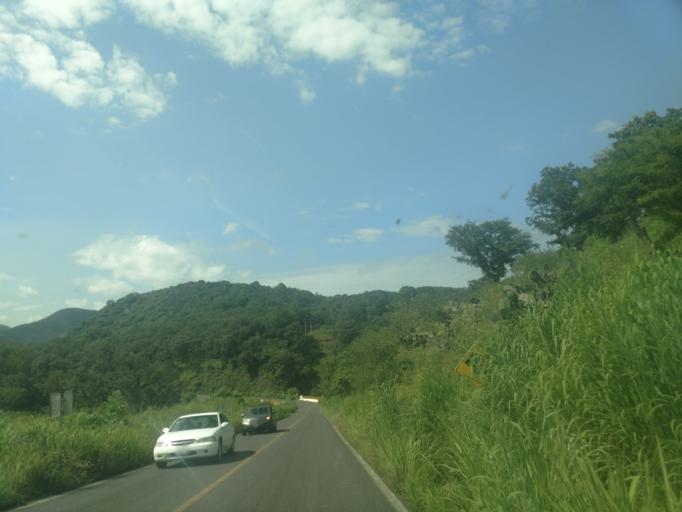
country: MX
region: Jalisco
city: Talpa de Allende
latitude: 20.4427
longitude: -104.7640
